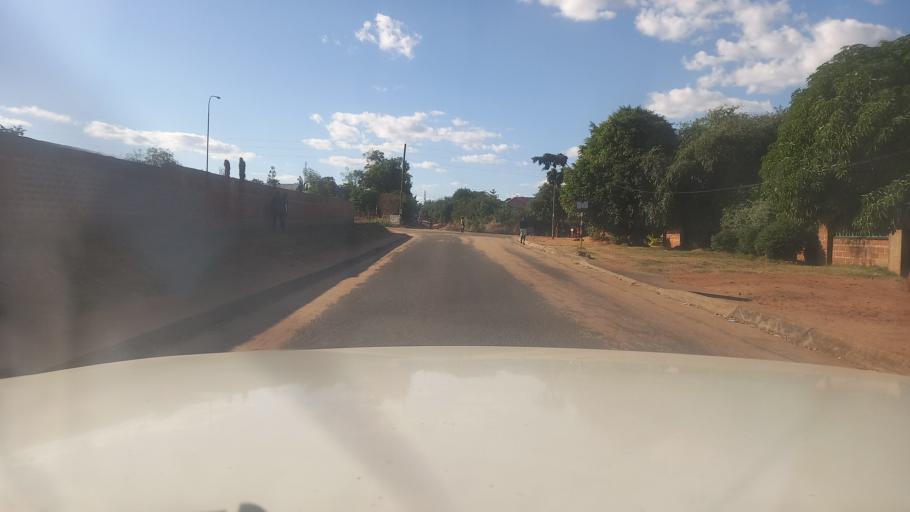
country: ZM
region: Southern
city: Livingstone
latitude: -17.8308
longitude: 25.8663
